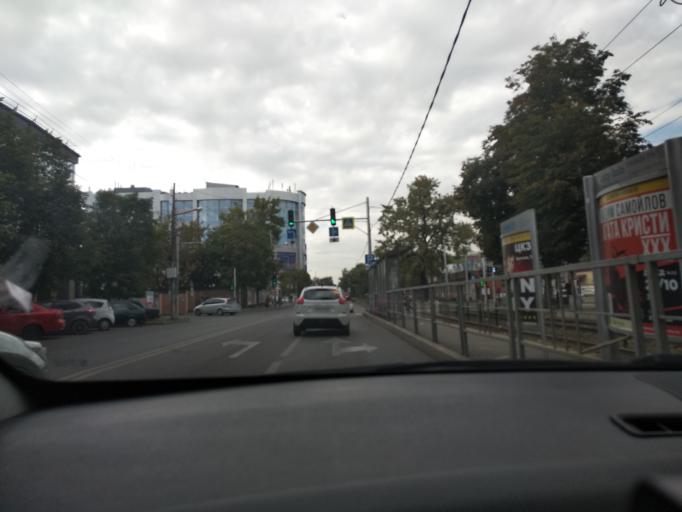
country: RU
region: Krasnodarskiy
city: Krasnodar
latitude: 45.0458
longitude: 38.9819
